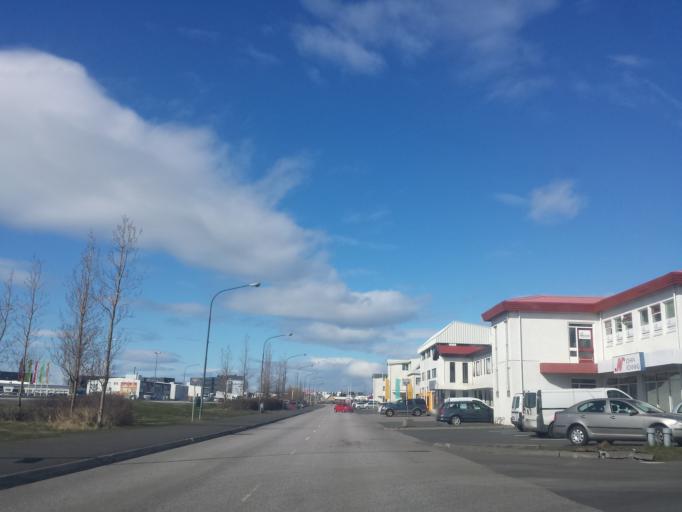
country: IS
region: Capital Region
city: Hafnarfjoerdur
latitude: 64.0788
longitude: -21.9404
